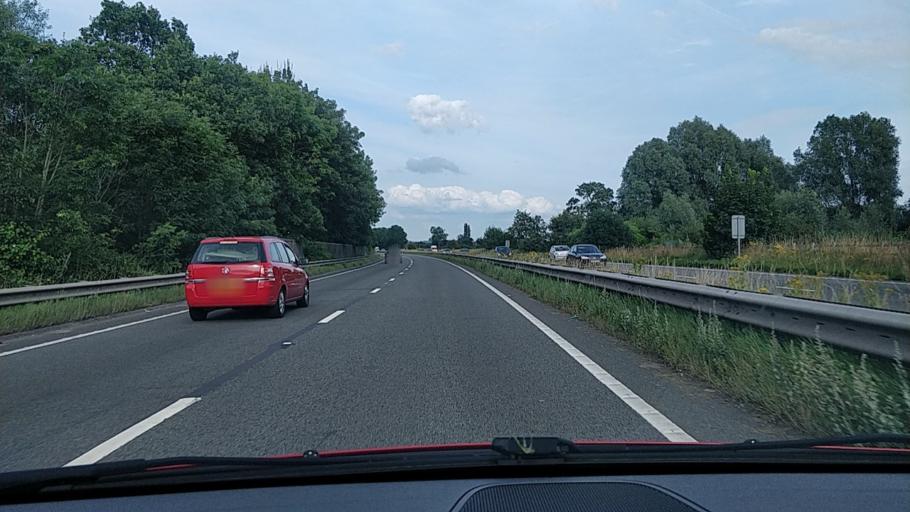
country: GB
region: Wales
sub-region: County of Flintshire
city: Hawarden
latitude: 53.1600
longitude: -2.9984
